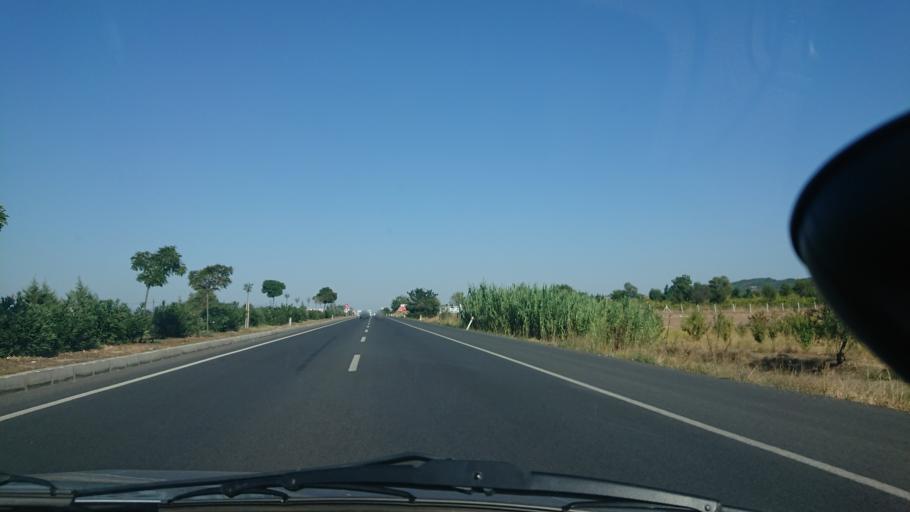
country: TR
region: Manisa
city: Ahmetli
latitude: 38.5065
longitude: 27.8901
